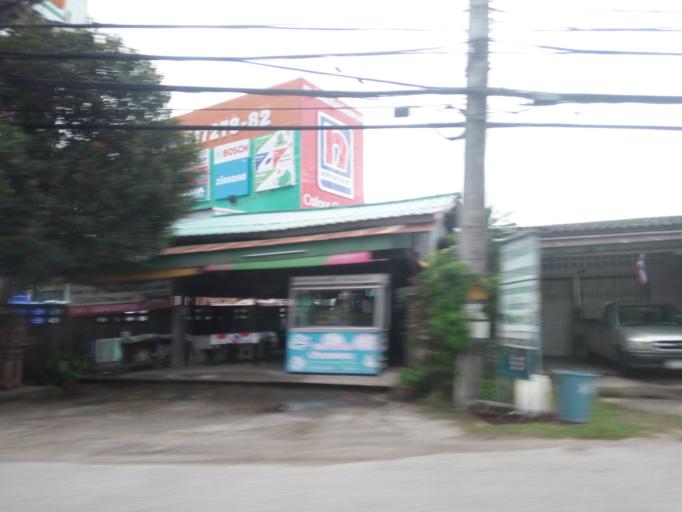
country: TH
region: Phuket
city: Thalang
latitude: 7.9978
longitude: 98.3497
